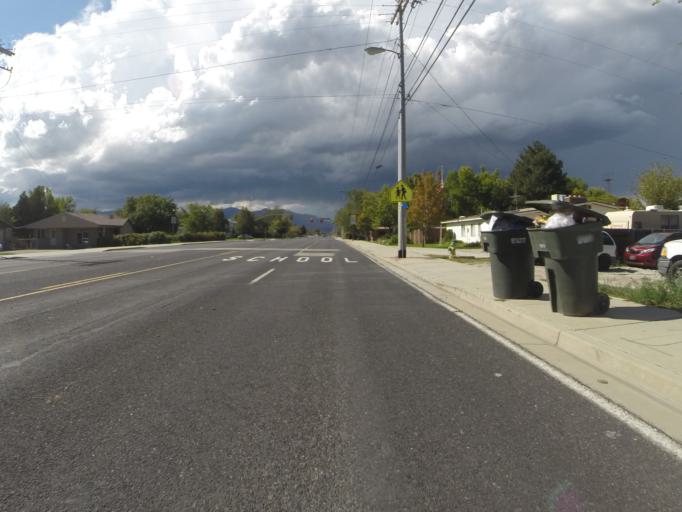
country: US
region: Utah
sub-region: Salt Lake County
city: West Valley City
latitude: 40.7040
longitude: -111.9722
